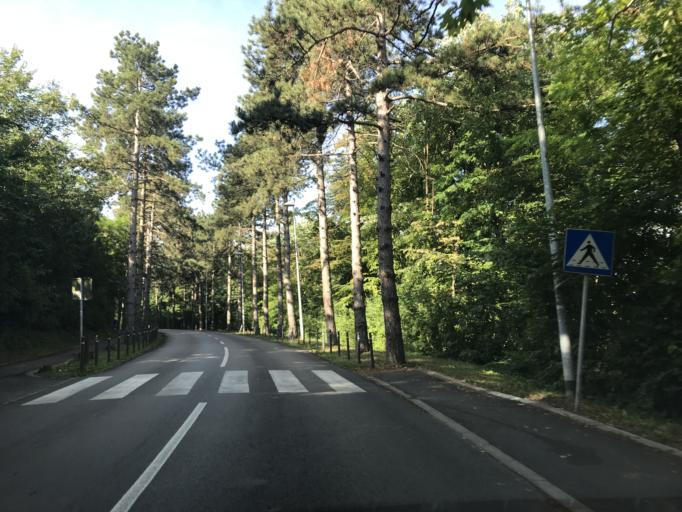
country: RS
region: Autonomna Pokrajina Vojvodina
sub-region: Juznobacki Okrug
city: Novi Sad
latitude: 45.2212
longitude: 19.8545
